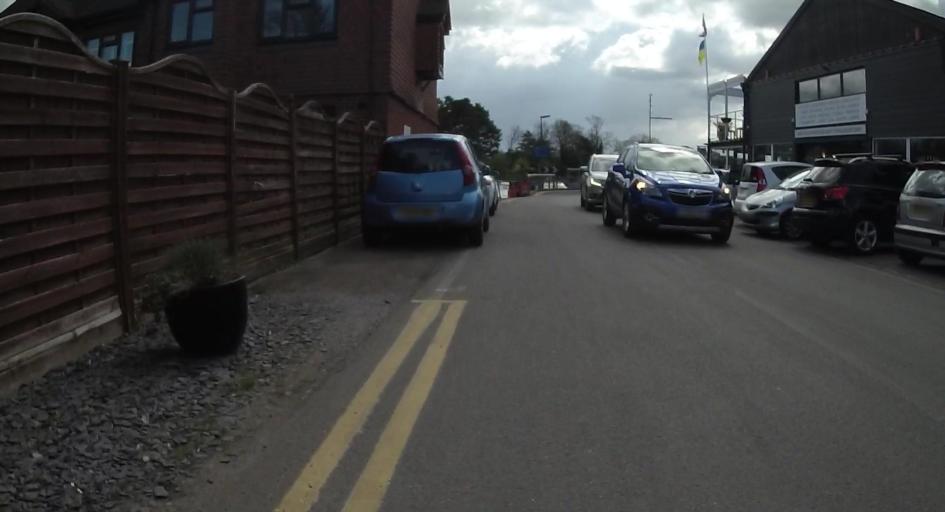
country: GB
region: England
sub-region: Surrey
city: Weybridge
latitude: 51.3831
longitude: -0.4573
